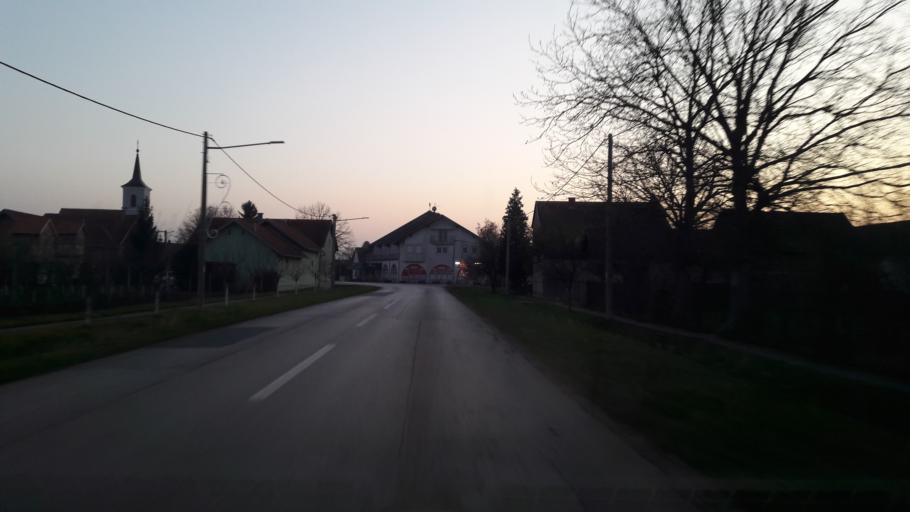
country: HR
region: Vukovarsko-Srijemska
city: Nijemci
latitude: 45.1834
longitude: 19.0129
